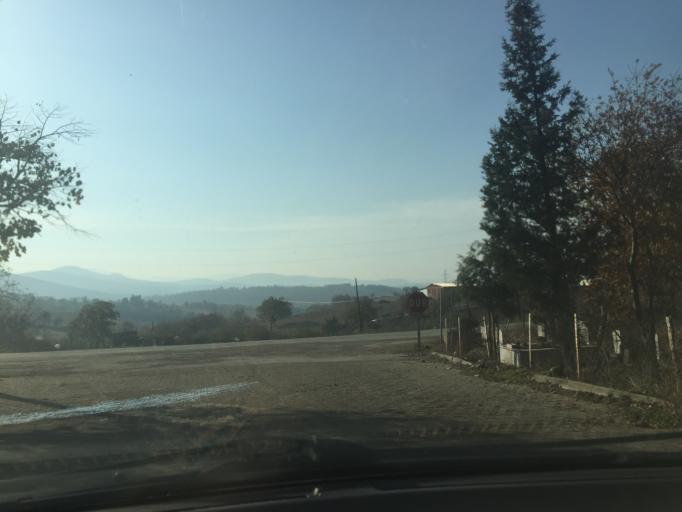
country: TR
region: Canakkale
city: Etili
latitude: 39.9408
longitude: 26.7943
